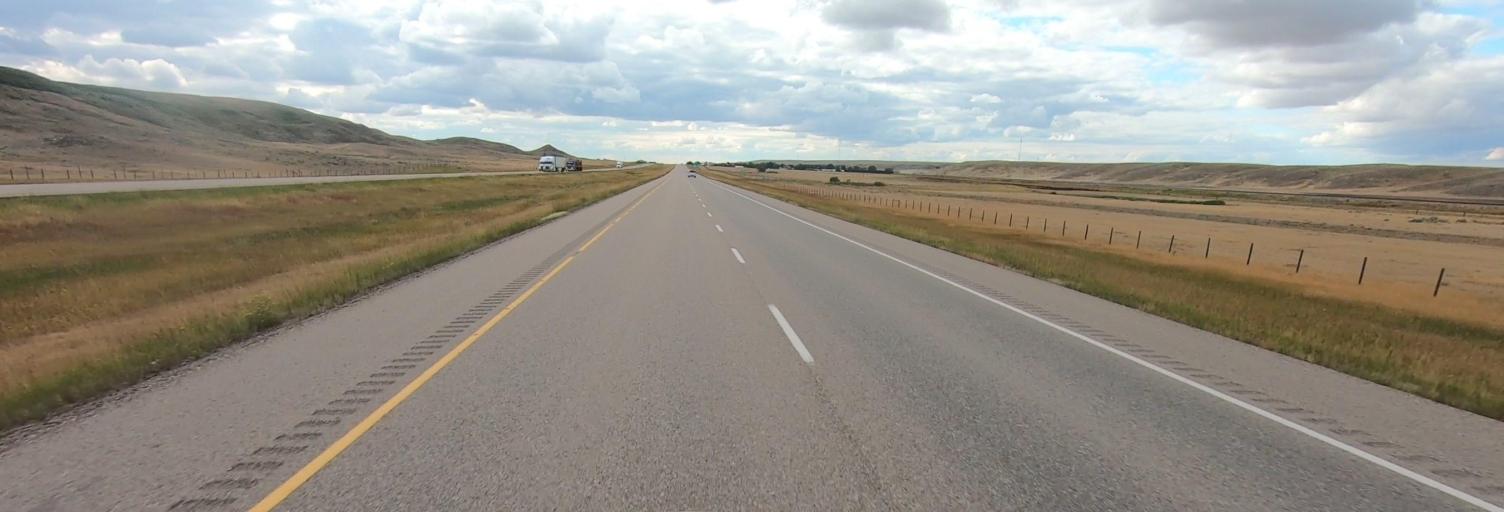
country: CA
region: Alberta
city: Medicine Hat
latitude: 49.9518
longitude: -110.2427
